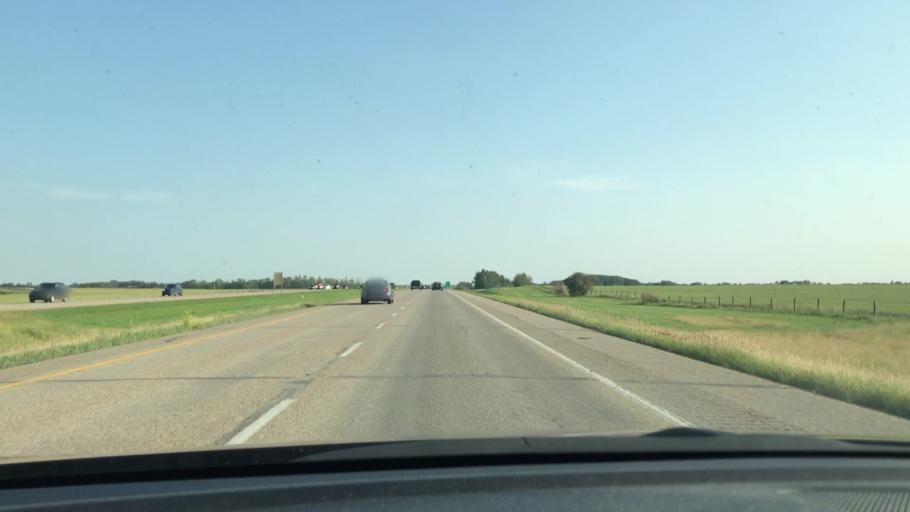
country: CA
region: Alberta
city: Millet
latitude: 53.1079
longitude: -113.5984
